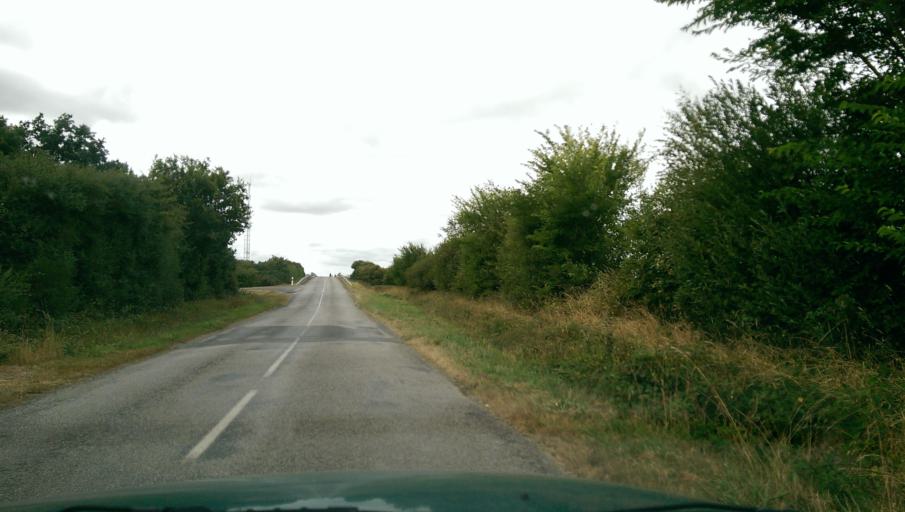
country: FR
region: Pays de la Loire
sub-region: Departement de la Loire-Atlantique
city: La Planche
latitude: 47.0316
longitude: -1.4032
